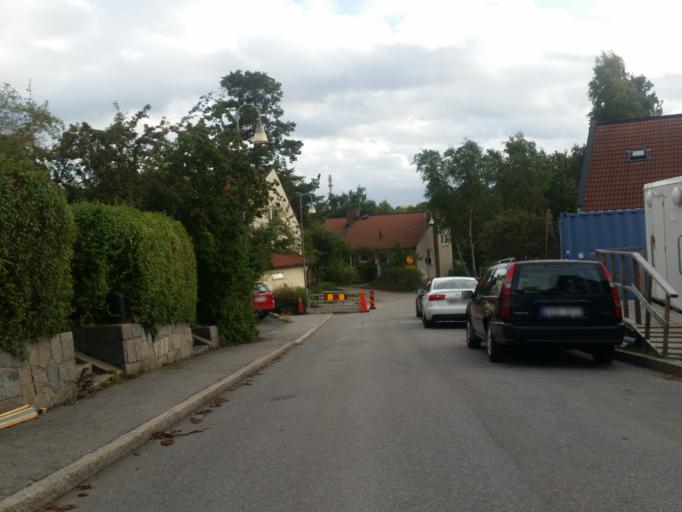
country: SE
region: Stockholm
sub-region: Stockholms Kommun
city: Arsta
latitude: 59.2559
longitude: 18.0985
